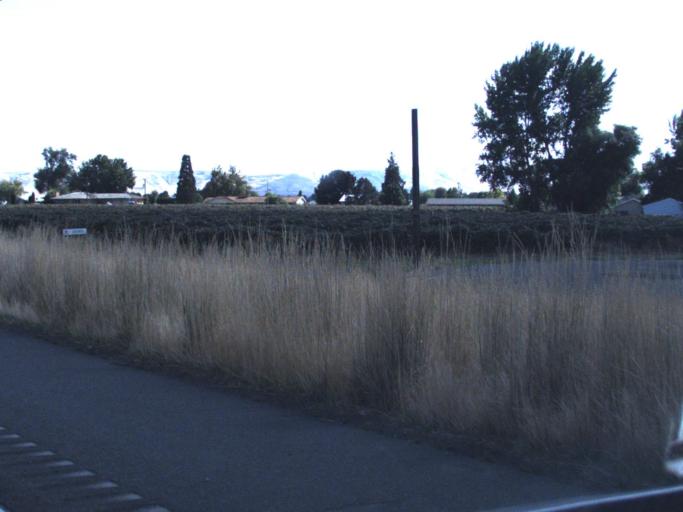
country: US
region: Washington
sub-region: Yakima County
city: Grandview
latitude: 46.2607
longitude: -119.8885
